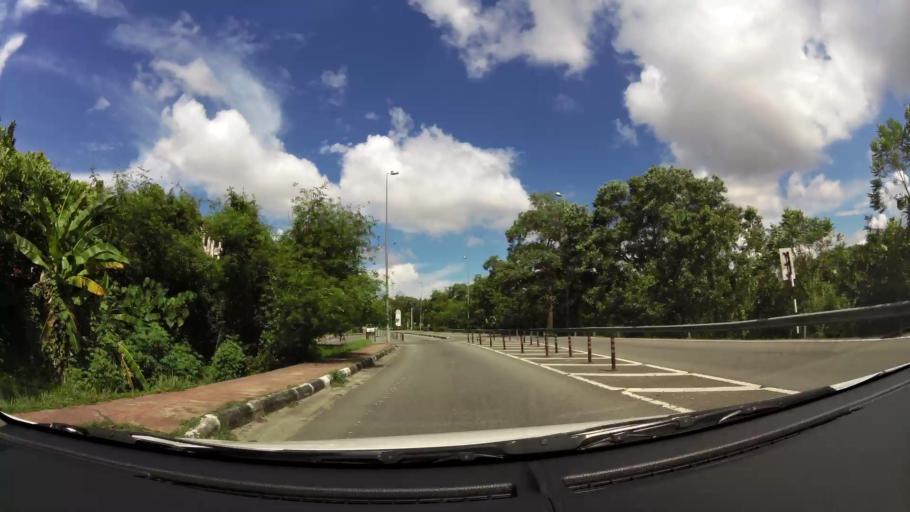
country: BN
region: Brunei and Muara
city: Bandar Seri Begawan
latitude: 4.9636
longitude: 114.9498
